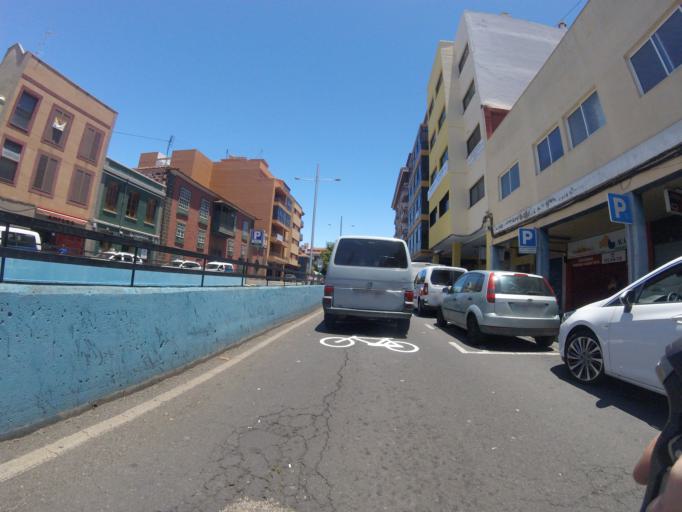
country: ES
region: Canary Islands
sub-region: Provincia de Santa Cruz de Tenerife
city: La Laguna
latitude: 28.4868
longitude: -16.3160
